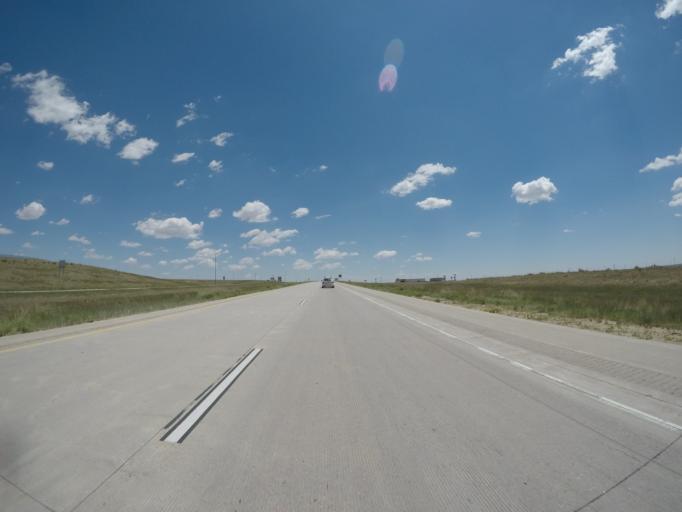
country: US
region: Colorado
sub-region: Lincoln County
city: Limon
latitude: 39.2732
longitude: -103.7203
